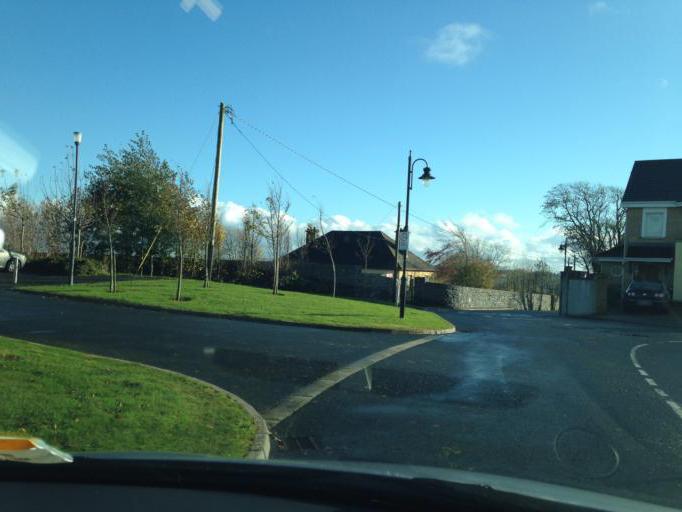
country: IE
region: Connaught
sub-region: County Galway
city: Oranmore
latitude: 53.2747
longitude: -8.9697
